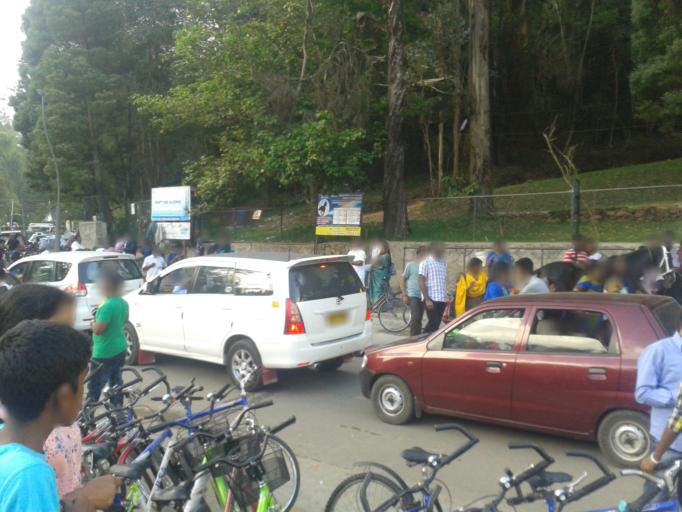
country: IN
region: Tamil Nadu
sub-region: Dindigul
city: Kodaikanal
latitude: 10.2321
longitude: 77.4912
